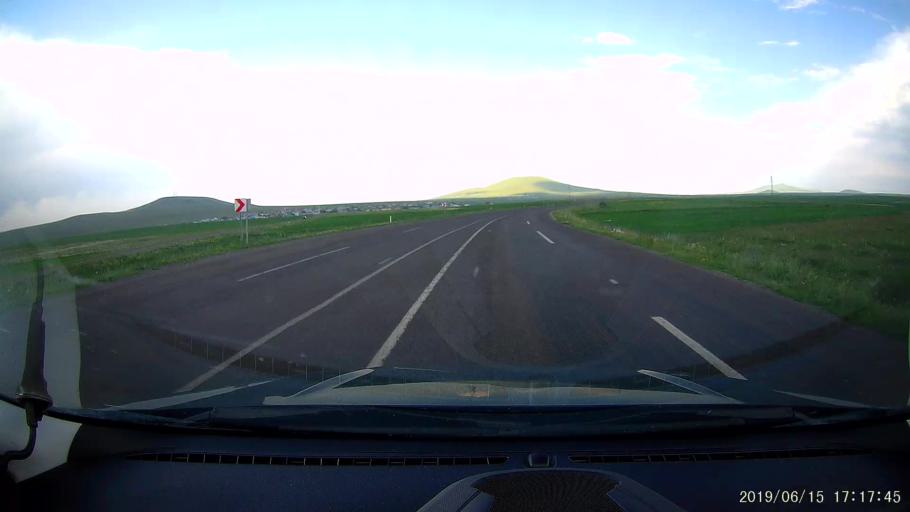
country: TR
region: Kars
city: Kars
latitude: 40.6151
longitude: 43.2447
